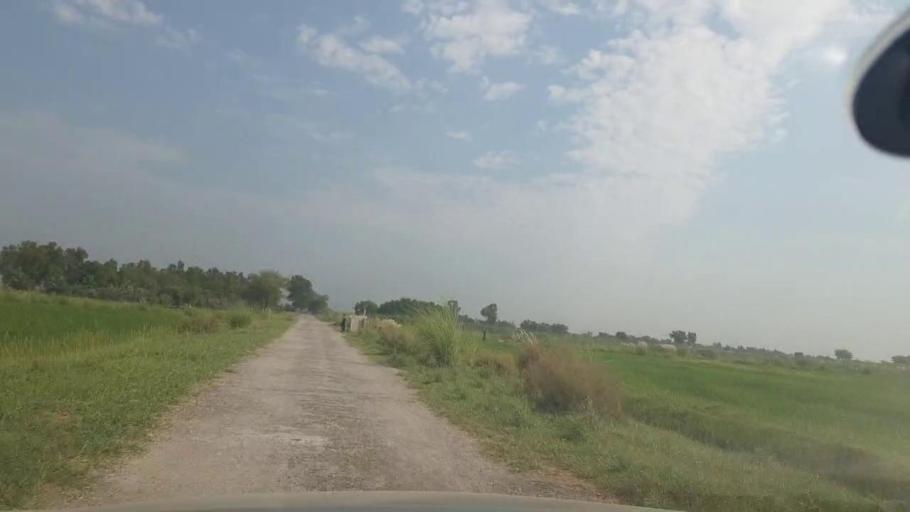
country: PK
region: Balochistan
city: Mehrabpur
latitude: 28.0504
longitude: 68.1229
